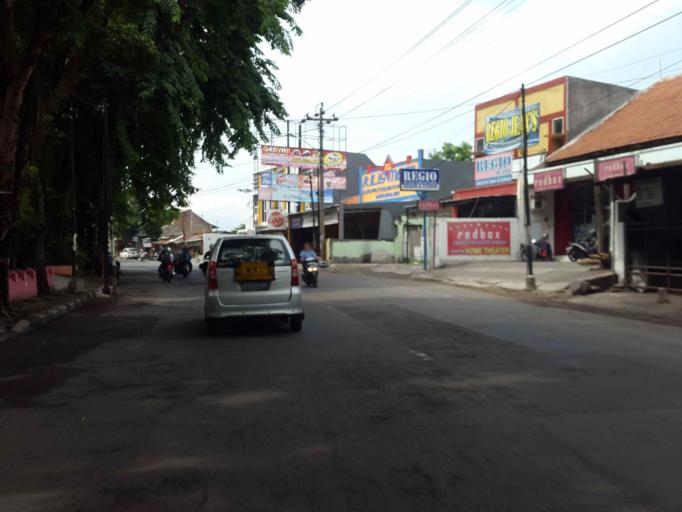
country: ID
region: Central Java
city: Semarang
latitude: -7.0054
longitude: 110.3965
